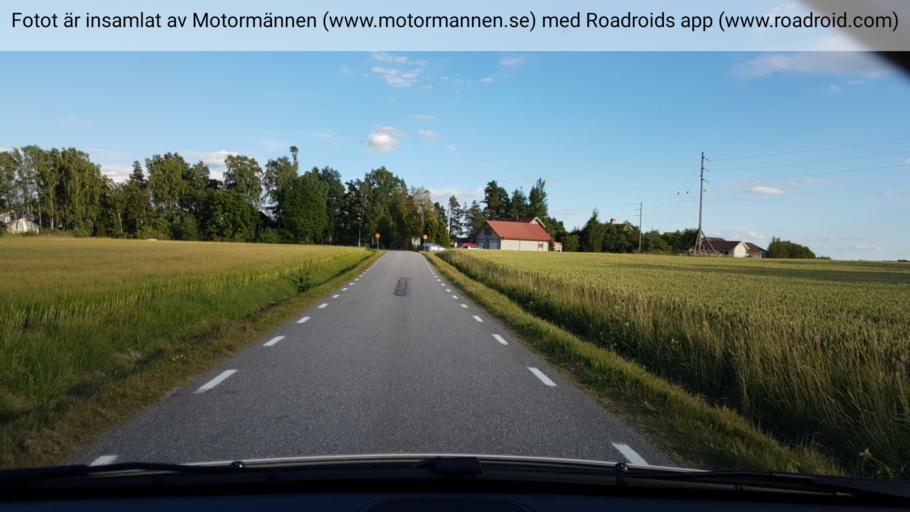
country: SE
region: Vaestmanland
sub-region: Vasteras
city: Tillberga
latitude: 59.6942
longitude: 16.6007
